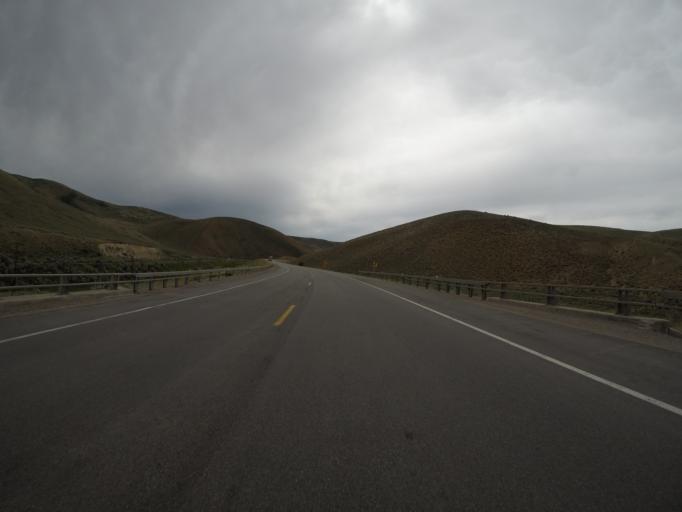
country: US
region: Wyoming
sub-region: Lincoln County
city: Kemmerer
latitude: 41.8258
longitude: -110.8145
